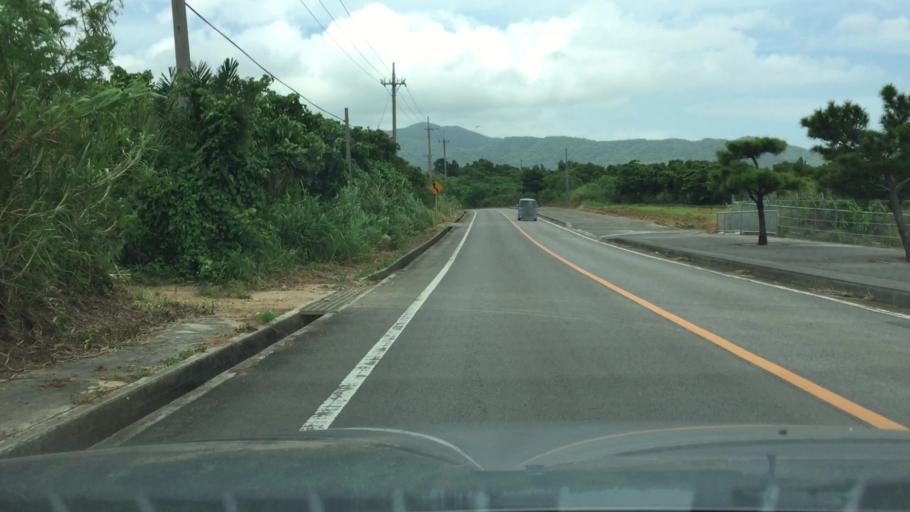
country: JP
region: Okinawa
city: Ishigaki
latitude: 24.4038
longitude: 124.2130
